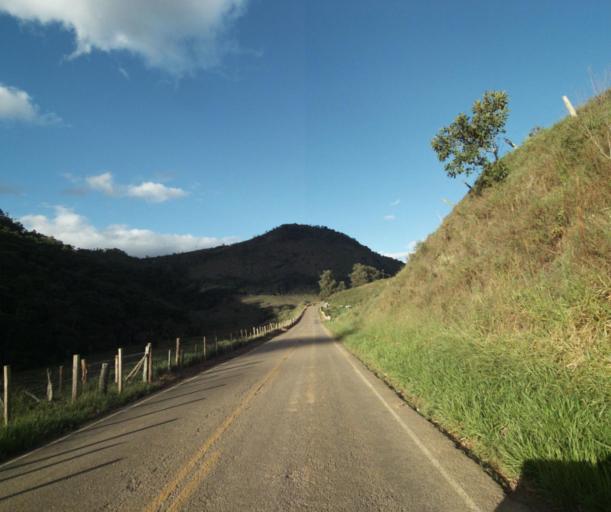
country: BR
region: Espirito Santo
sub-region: Guacui
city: Guacui
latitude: -20.6154
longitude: -41.6785
